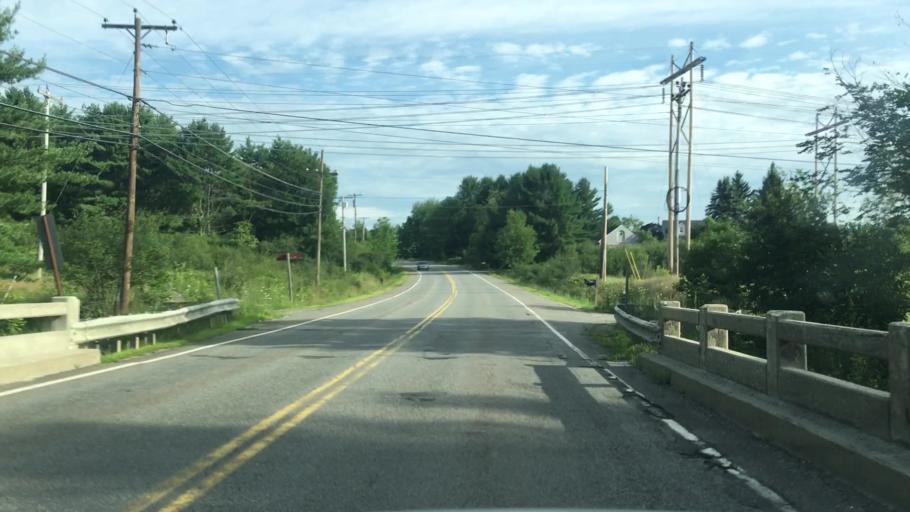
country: US
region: Maine
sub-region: Cumberland County
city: Gorham
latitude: 43.6436
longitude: -70.4216
